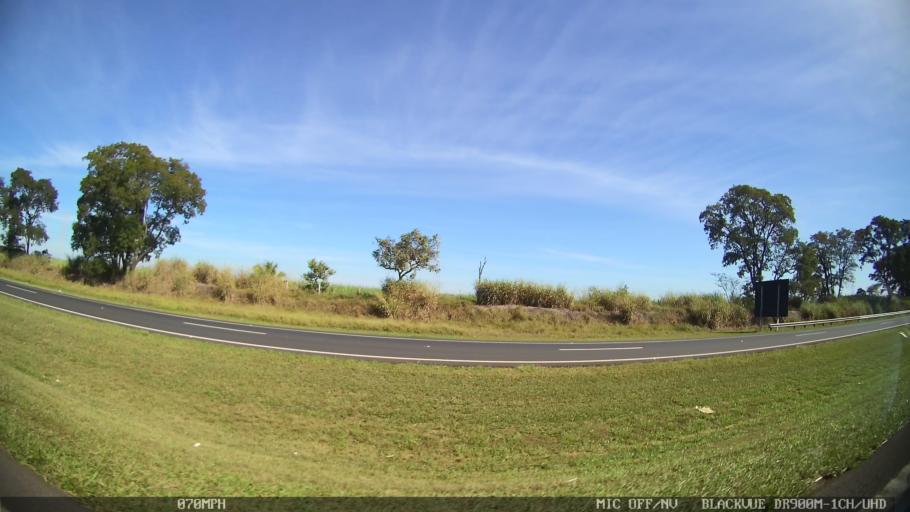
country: BR
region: Sao Paulo
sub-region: Porto Ferreira
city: Porto Ferreira
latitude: -21.9026
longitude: -47.4782
